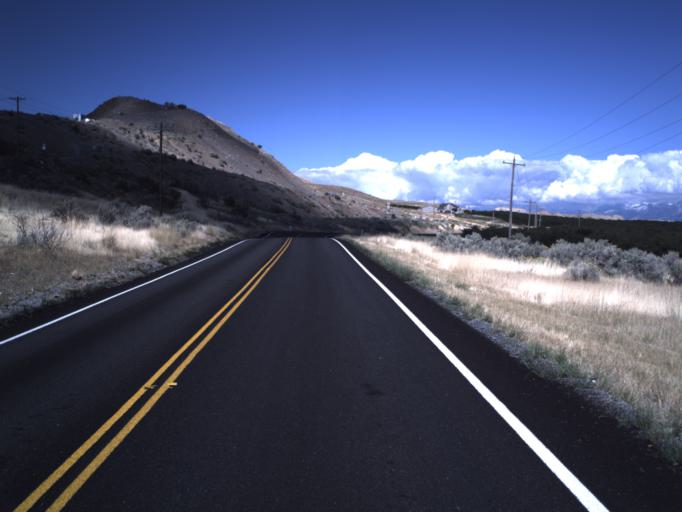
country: US
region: Utah
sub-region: Utah County
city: Santaquin
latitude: 40.0084
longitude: -111.8026
